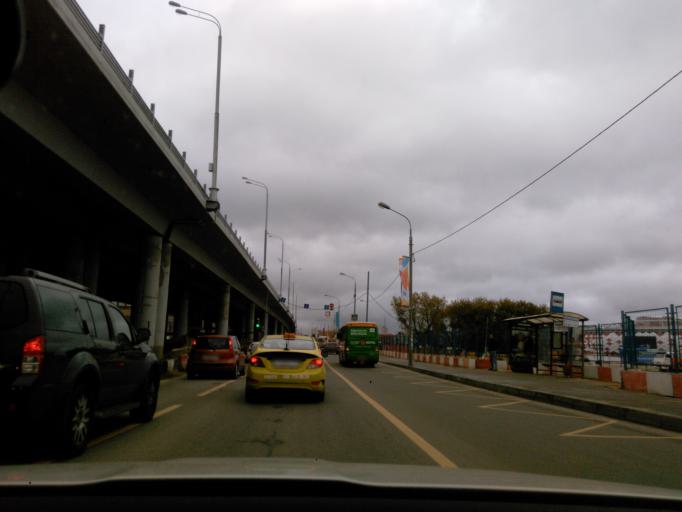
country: RU
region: Moscow
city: Strogino
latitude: 55.8247
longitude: 37.4322
